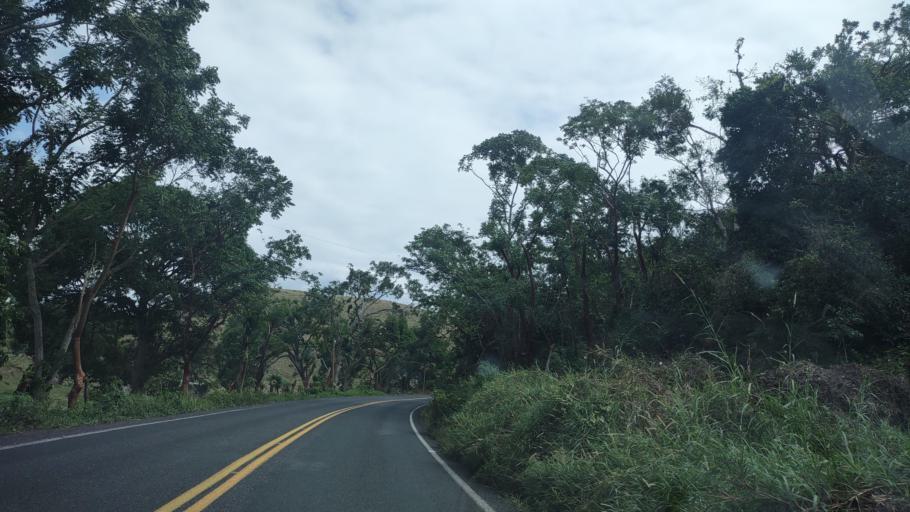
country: MX
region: Veracruz
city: Papantla de Olarte
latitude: 20.4641
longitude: -97.2739
